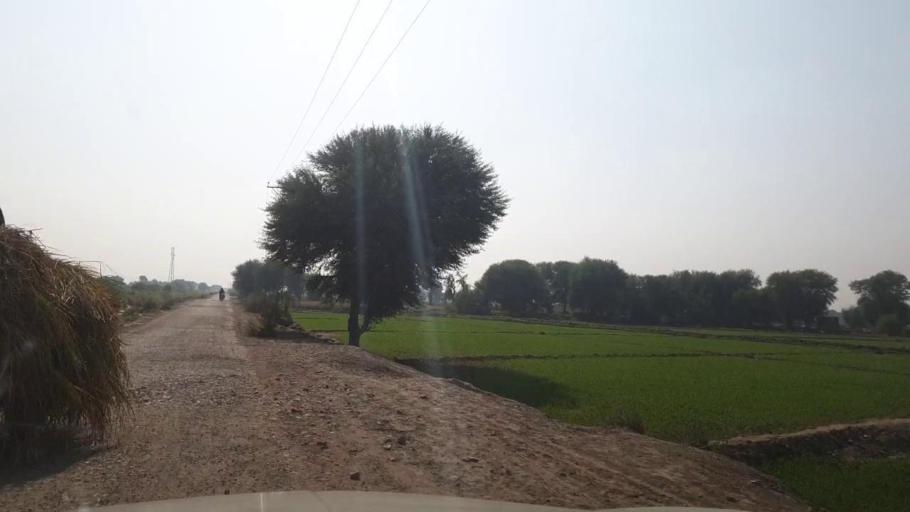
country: PK
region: Sindh
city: Bhan
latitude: 26.5343
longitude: 67.7766
